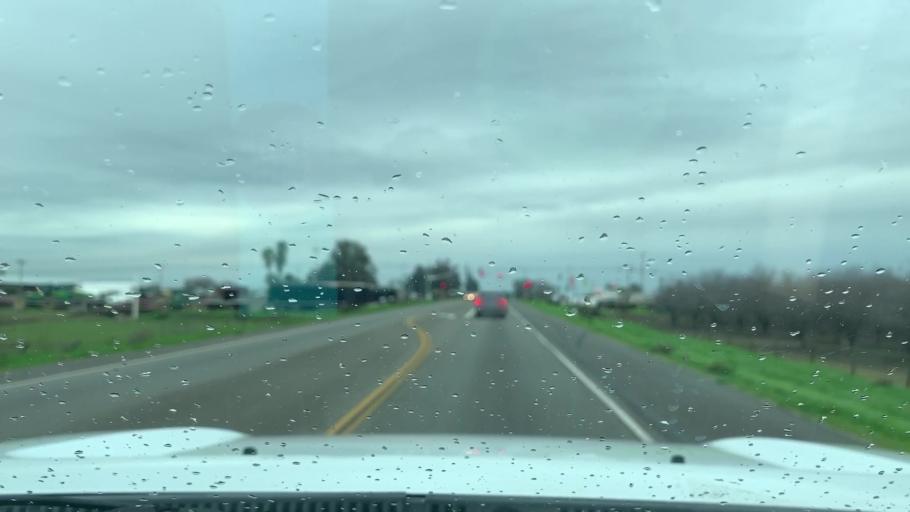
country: US
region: California
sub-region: Fresno County
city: Riverdale
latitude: 36.4291
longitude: -119.8016
